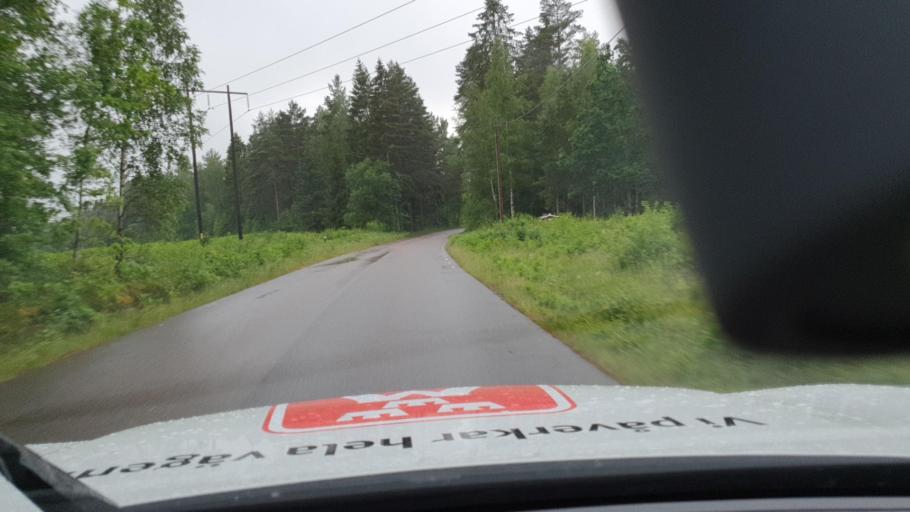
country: SE
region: Vaestra Goetaland
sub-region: Skovde Kommun
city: Stopen
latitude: 58.4286
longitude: 13.9202
